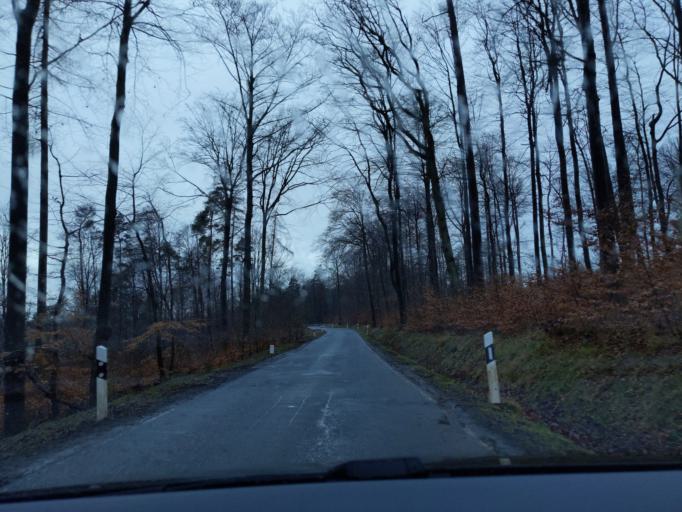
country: DE
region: Hesse
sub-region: Regierungsbezirk Kassel
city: Bad Arolsen
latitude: 51.3261
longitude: 9.0321
